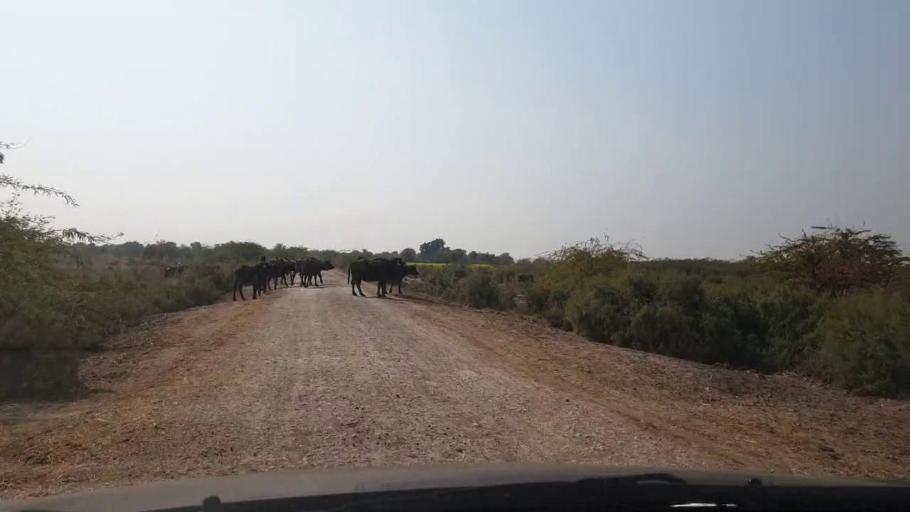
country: PK
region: Sindh
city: Jhol
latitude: 25.8834
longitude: 68.9842
